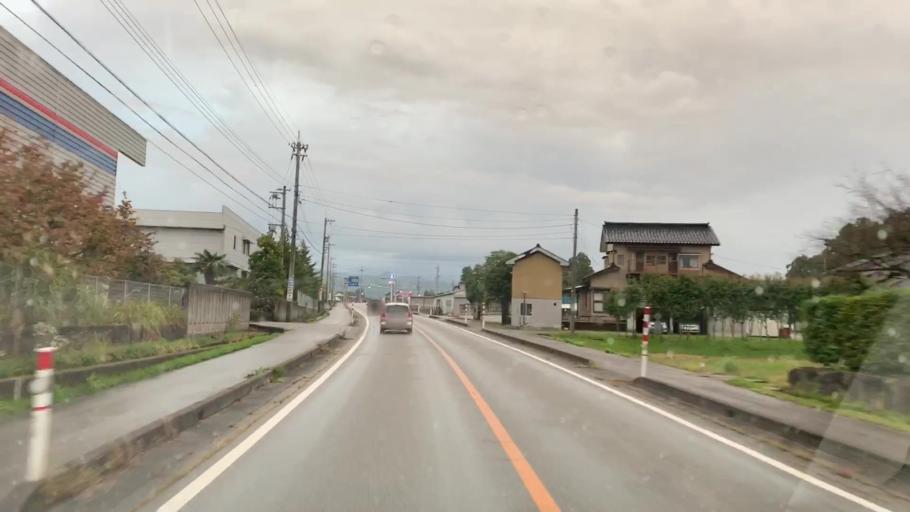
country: JP
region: Toyama
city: Kamiichi
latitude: 36.6553
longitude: 137.3283
